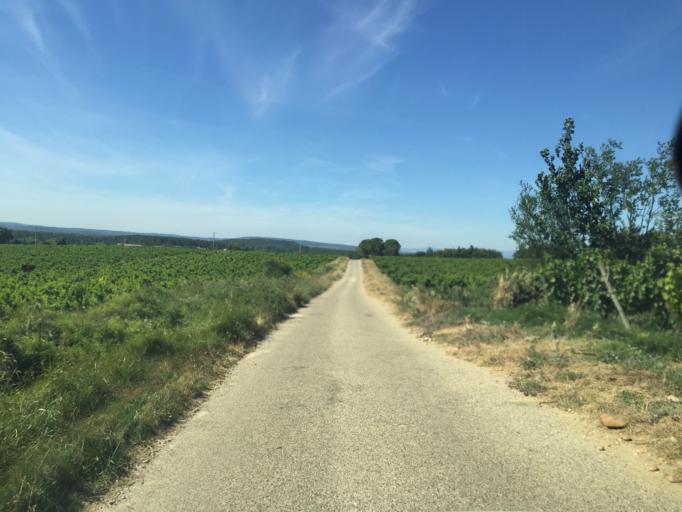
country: FR
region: Provence-Alpes-Cote d'Azur
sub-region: Departement du Vaucluse
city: Chateauneuf-du-Pape
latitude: 44.0896
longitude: 4.8047
